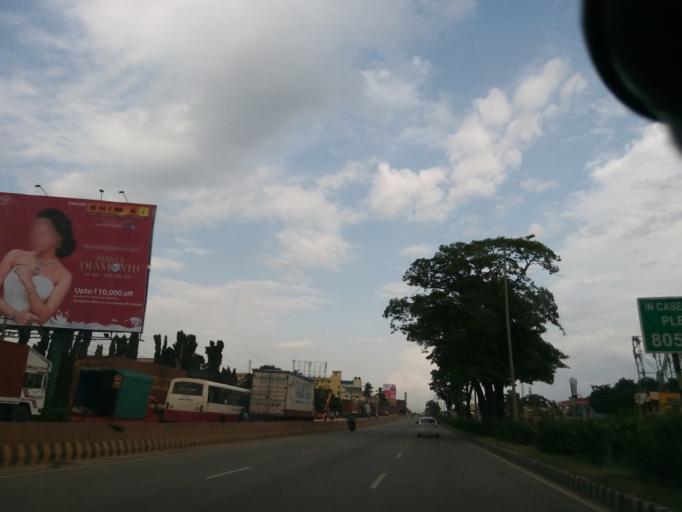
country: IN
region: Karnataka
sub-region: Bangalore Rural
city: Nelamangala
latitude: 13.0638
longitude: 77.4567
